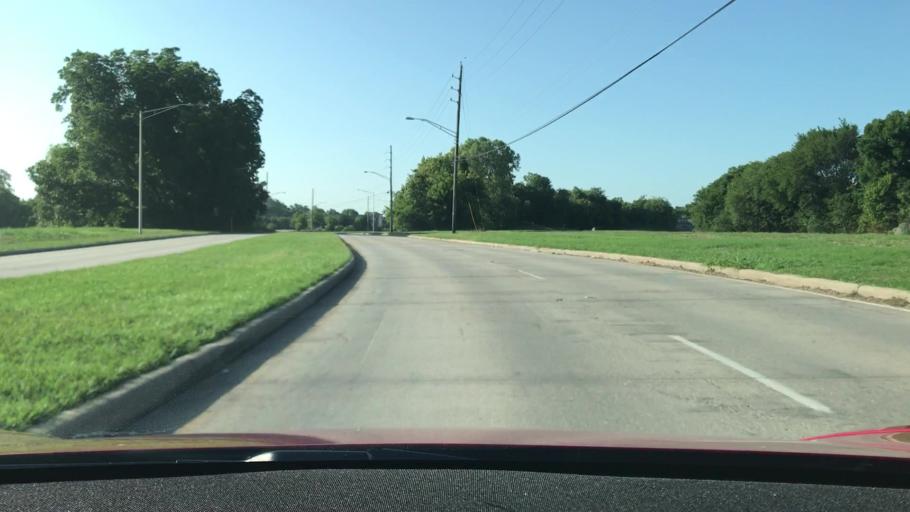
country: US
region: Louisiana
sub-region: Bossier Parish
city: Bossier City
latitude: 32.4360
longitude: -93.7284
